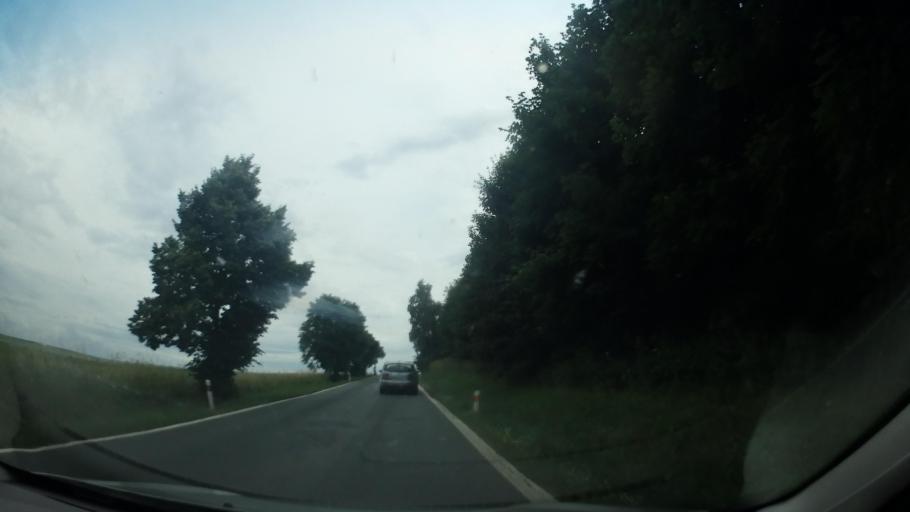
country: CZ
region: Vysocina
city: Bystrice nad Pernstejnem
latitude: 49.5084
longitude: 16.1662
